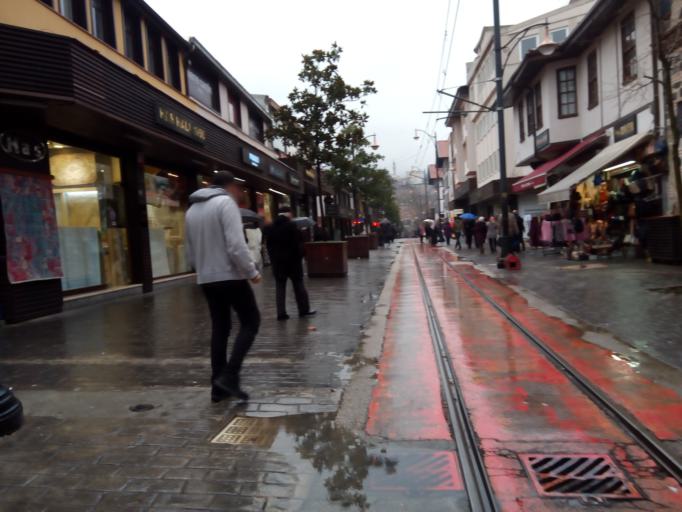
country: TR
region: Bursa
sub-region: Osmangazi
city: Bursa
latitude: 40.1859
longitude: 29.0629
